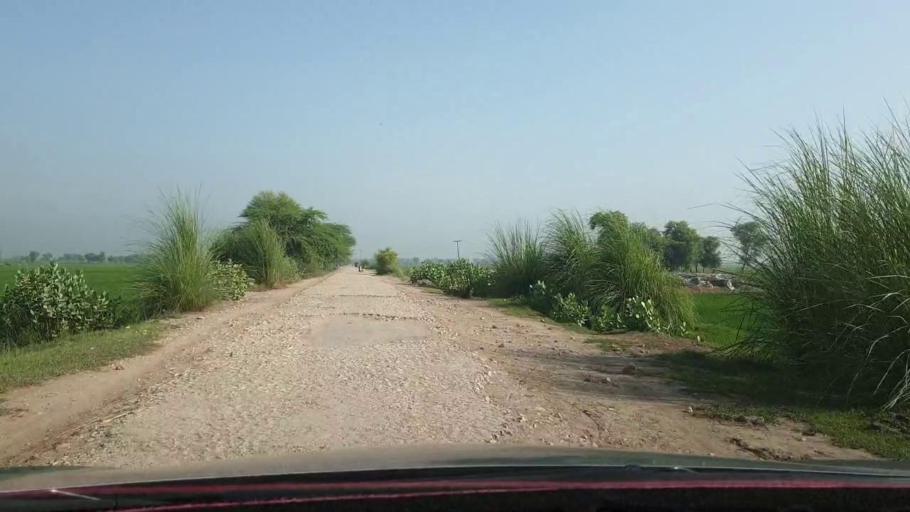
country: PK
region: Sindh
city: Nasirabad
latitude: 27.4352
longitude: 67.9204
